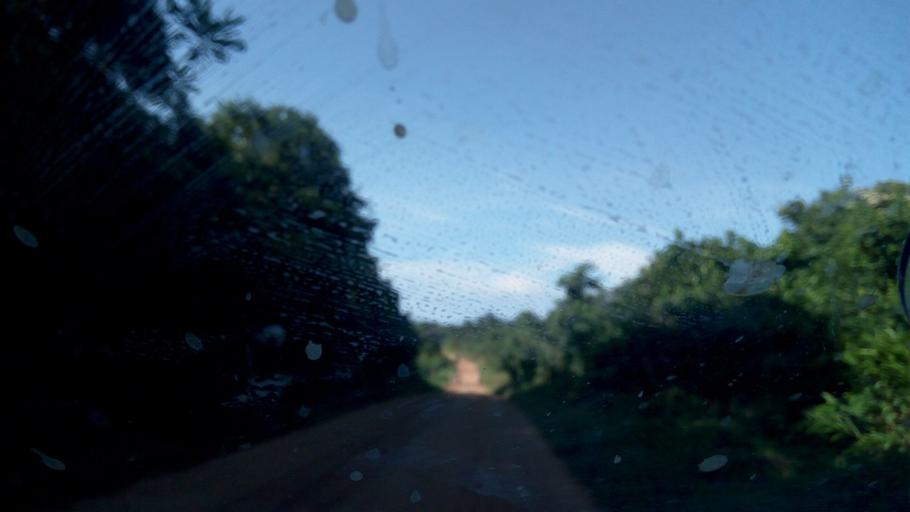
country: BI
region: Bururi
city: Rumonge
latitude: -4.3453
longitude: 28.9364
